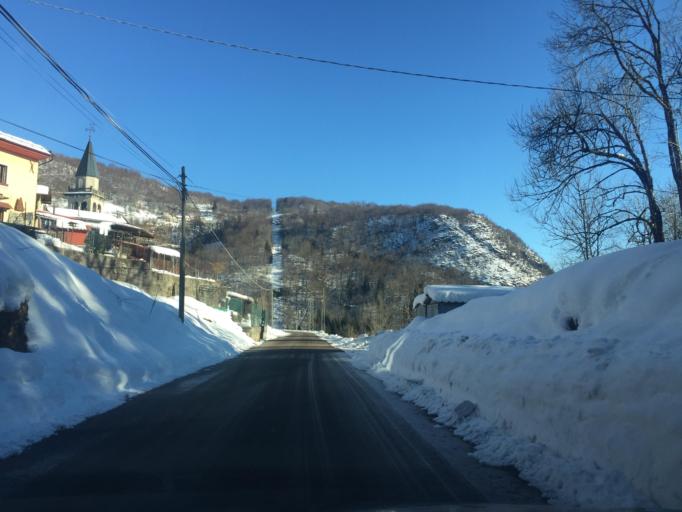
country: IT
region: Friuli Venezia Giulia
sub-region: Provincia di Udine
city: Lauco
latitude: 46.4401
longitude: 12.9473
